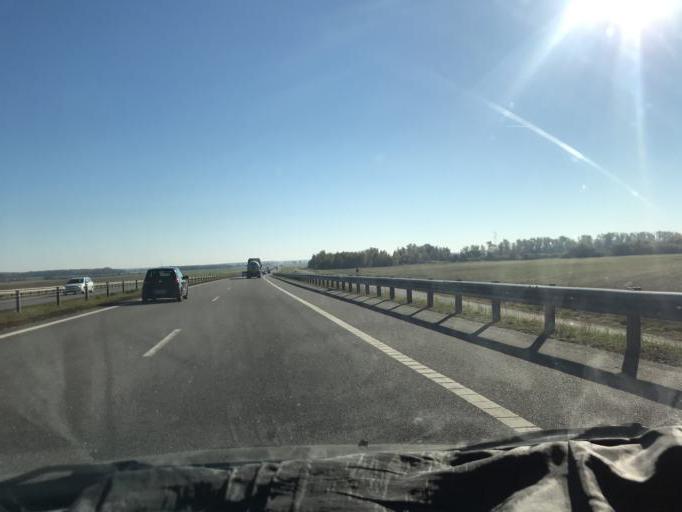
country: BY
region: Mogilev
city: Yalizava
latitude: 53.2461
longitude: 28.9373
